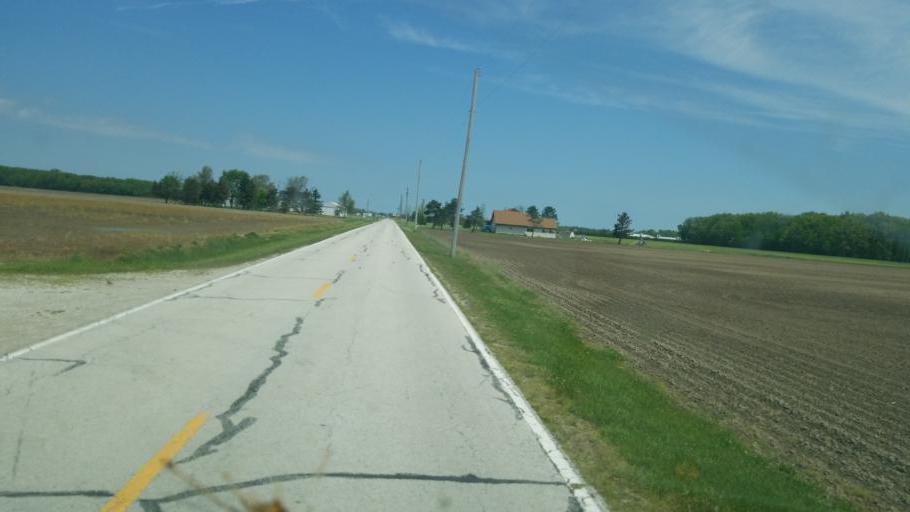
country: US
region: Ohio
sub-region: Ottawa County
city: Oak Harbor
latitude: 41.4533
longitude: -83.2017
